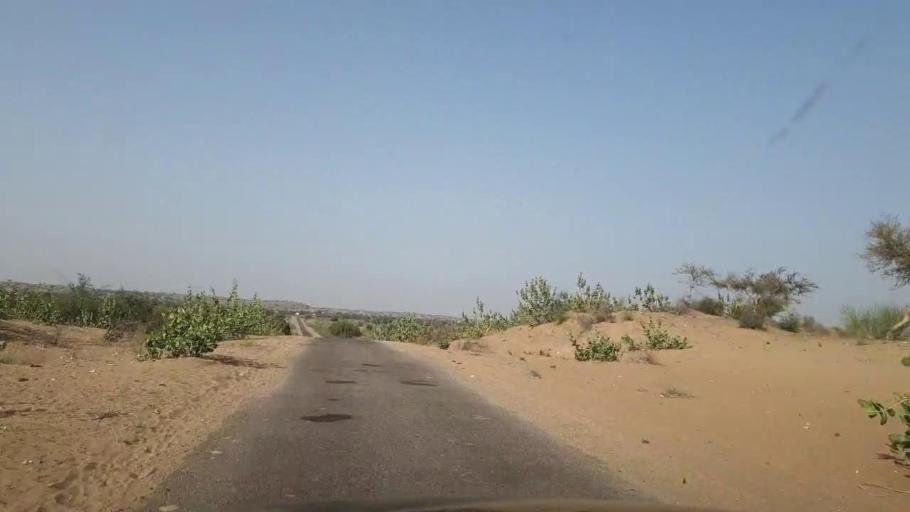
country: PK
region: Sindh
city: Islamkot
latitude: 25.1485
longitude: 70.5197
